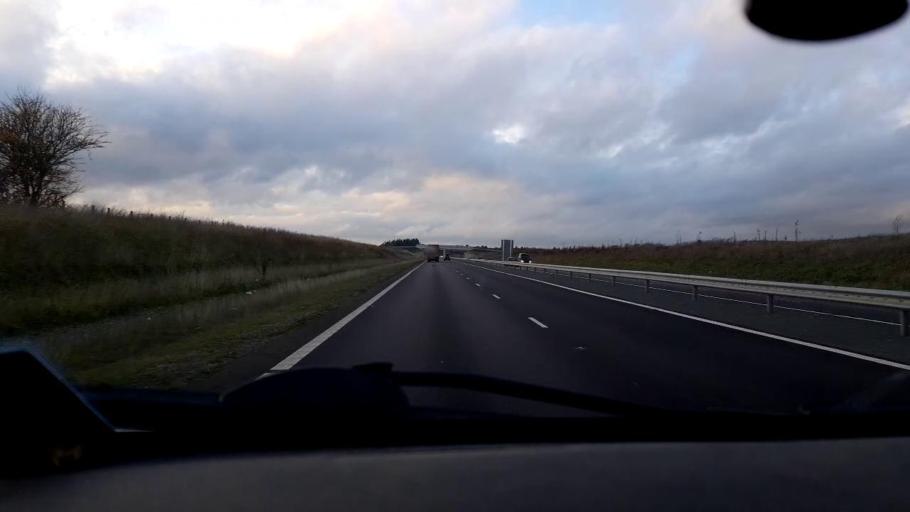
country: GB
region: England
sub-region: Norfolk
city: Horsford
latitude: 52.6907
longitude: 1.2307
